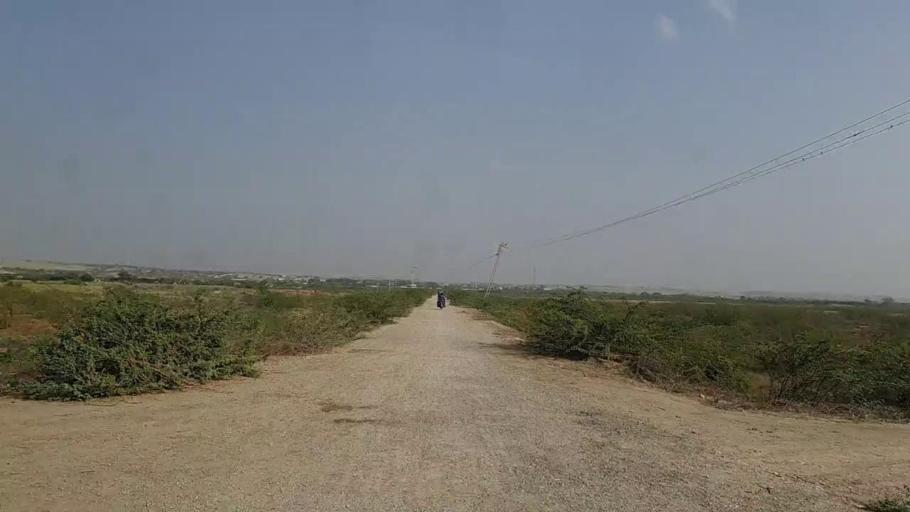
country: PK
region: Sindh
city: Naukot
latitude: 24.6644
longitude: 69.2803
